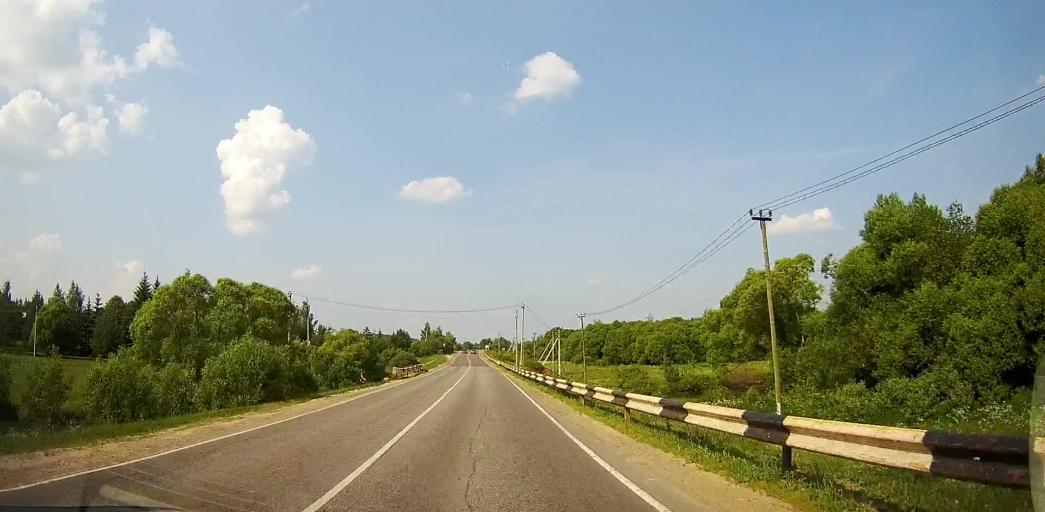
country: RU
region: Moskovskaya
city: Mikhnevo
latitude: 55.1817
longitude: 37.9740
